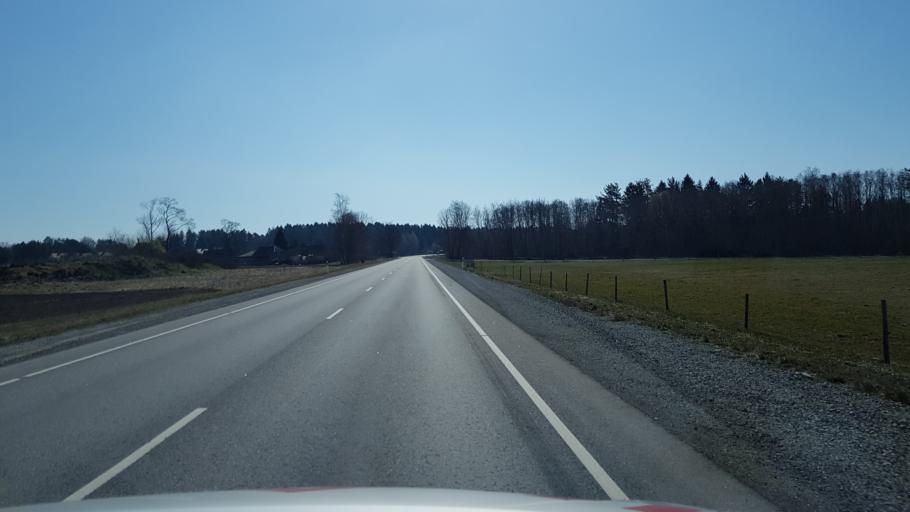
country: EE
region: Ida-Virumaa
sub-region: Kohtla-Jaerve linn
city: Kohtla-Jarve
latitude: 59.3386
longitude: 27.2570
